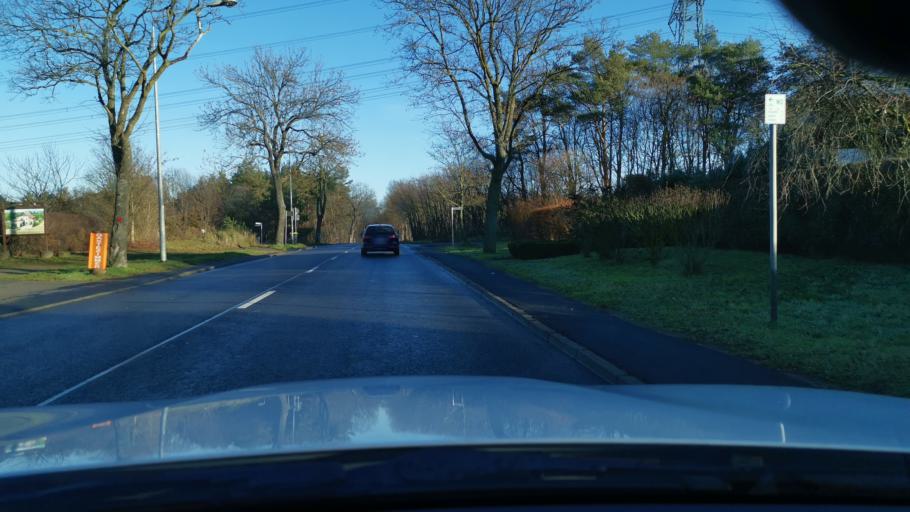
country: DE
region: Saxony-Anhalt
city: Abtsdorf
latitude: 51.9007
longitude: 12.6760
